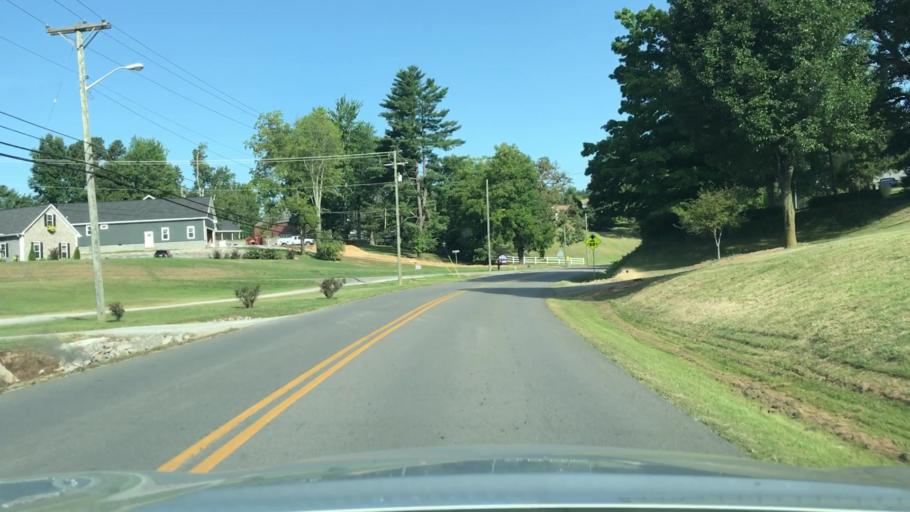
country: US
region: Kentucky
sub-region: Muhlenberg County
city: Greenville
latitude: 37.1956
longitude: -87.1758
